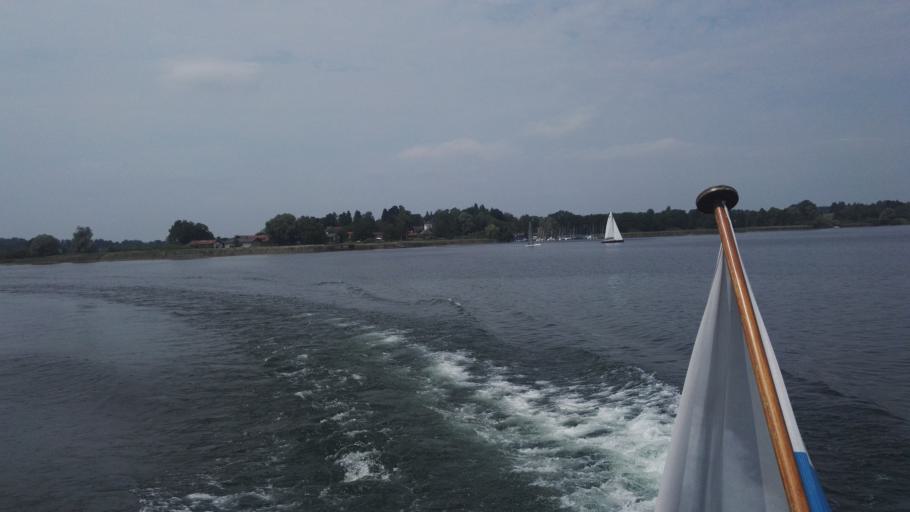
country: DE
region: Bavaria
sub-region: Upper Bavaria
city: Chiemsee
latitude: 47.8735
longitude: 12.3947
